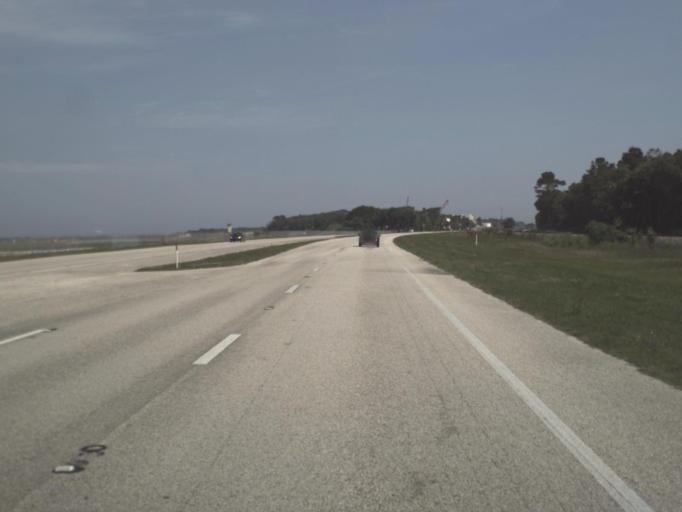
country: US
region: Florida
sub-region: Saint Johns County
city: Villano Beach
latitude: 29.9692
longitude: -81.3533
